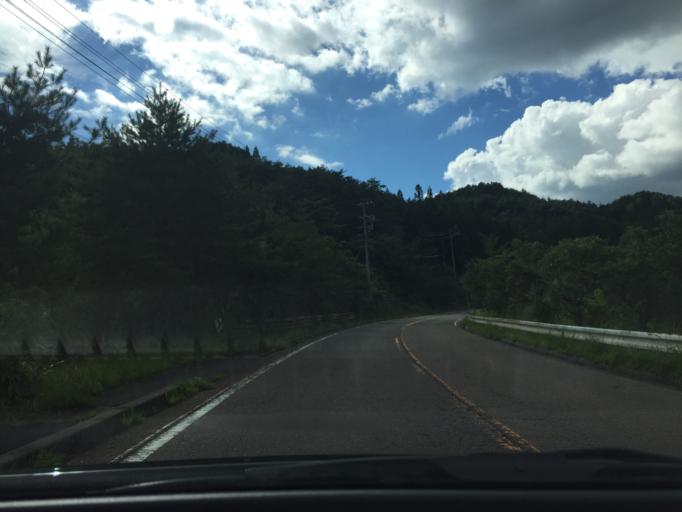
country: JP
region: Gifu
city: Nakatsugawa
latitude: 35.7449
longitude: 137.3325
